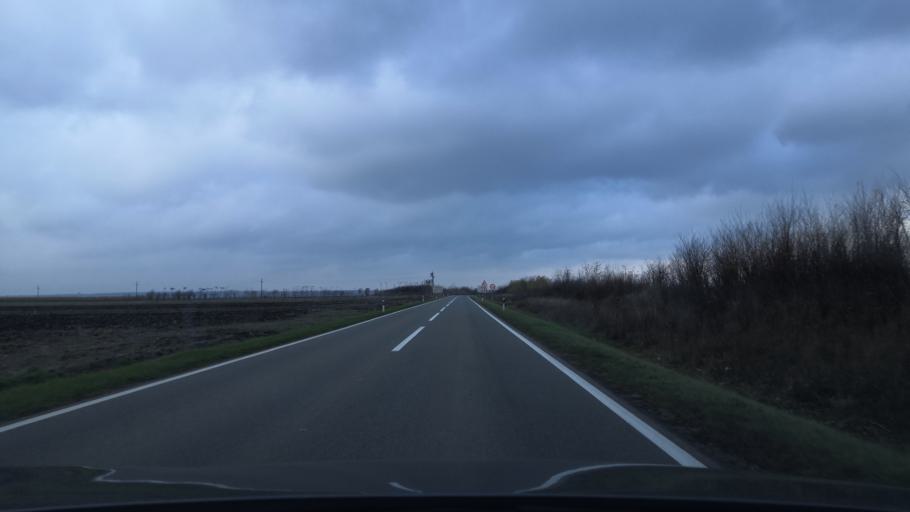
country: RS
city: Sanad
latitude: 45.9972
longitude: 20.1043
